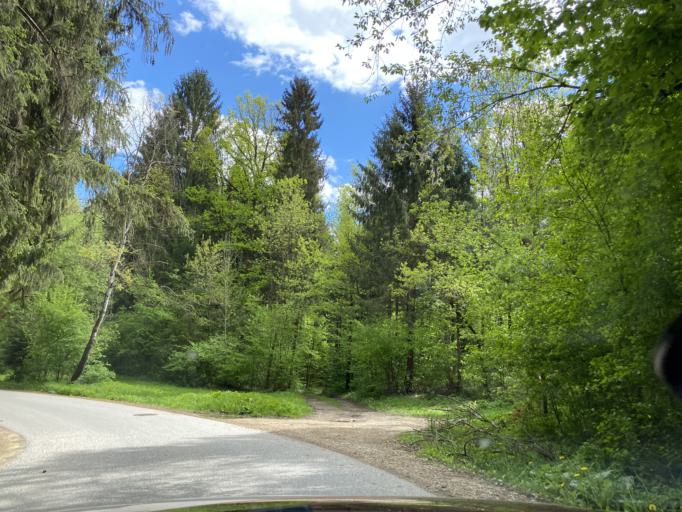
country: AT
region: Carinthia
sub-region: Politischer Bezirk Wolfsberg
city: Sankt Andrae
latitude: 46.7844
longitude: 14.8321
